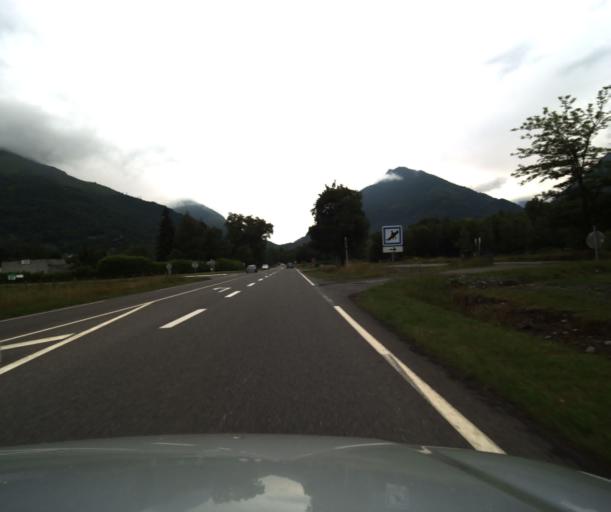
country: FR
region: Midi-Pyrenees
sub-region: Departement des Hautes-Pyrenees
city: Pierrefitte-Nestalas
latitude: 42.9801
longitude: -0.0698
